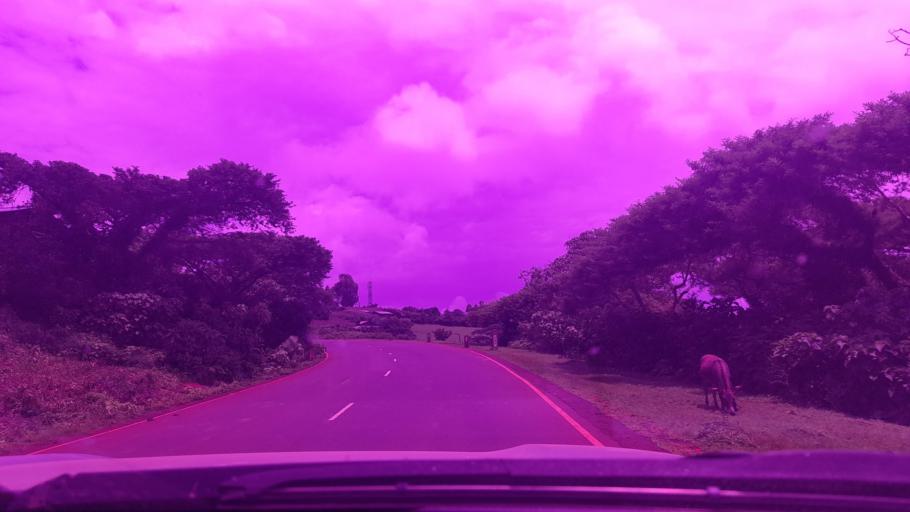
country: ET
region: Oromiya
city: Metu
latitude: 8.3363
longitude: 35.7372
